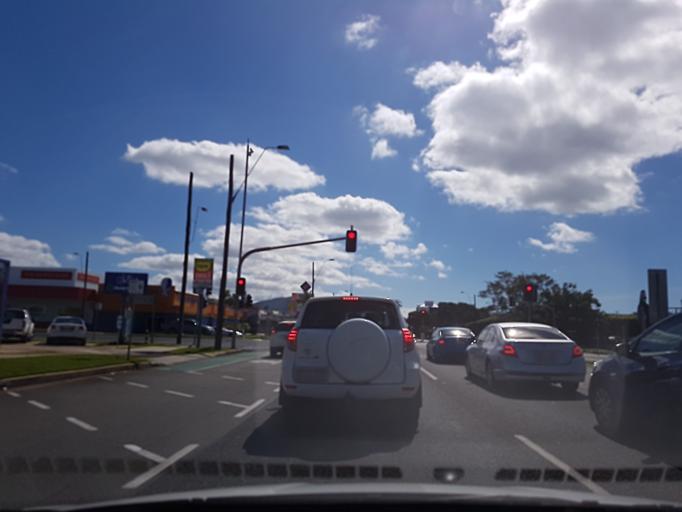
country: AU
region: Queensland
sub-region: Cairns
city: Cairns
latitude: -16.9207
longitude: 145.7711
